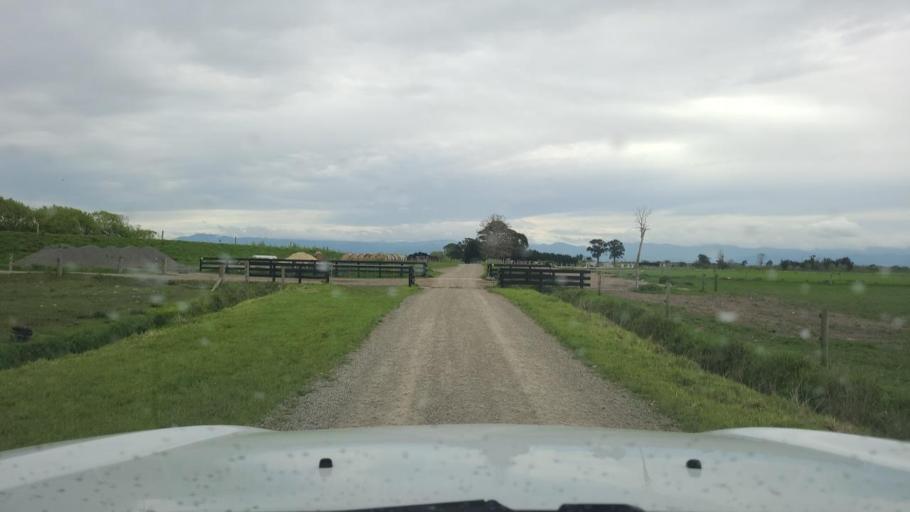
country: NZ
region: Wellington
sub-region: South Wairarapa District
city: Waipawa
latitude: -41.2558
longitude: 175.3679
